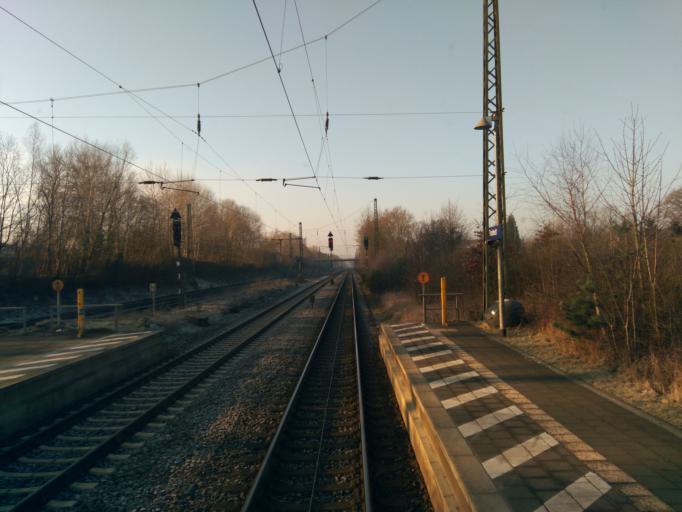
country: DE
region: Lower Saxony
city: Tostedt
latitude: 53.2717
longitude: 9.7305
